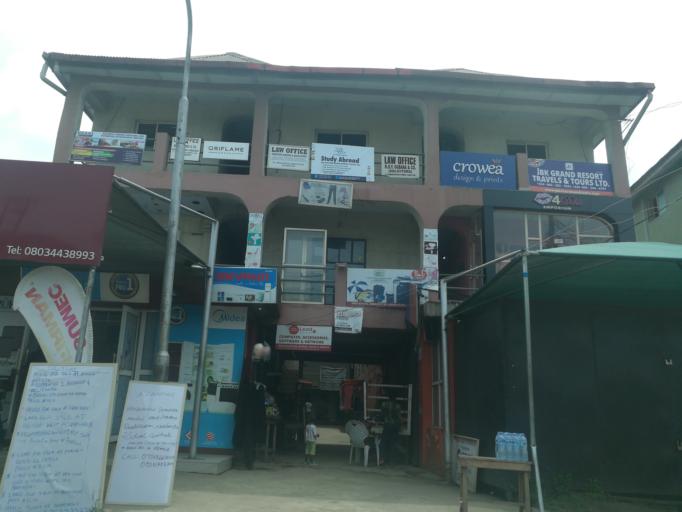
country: NG
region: Lagos
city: Ikorodu
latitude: 6.6162
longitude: 3.5024
